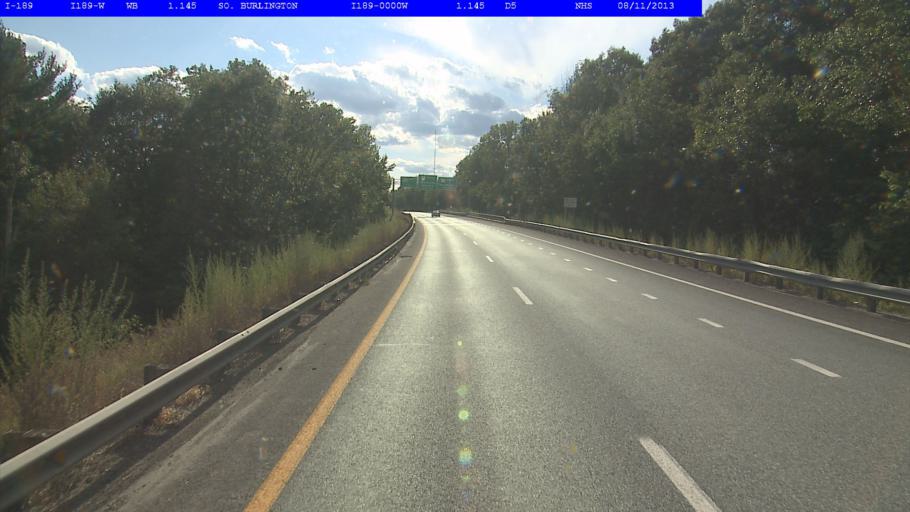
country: US
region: Vermont
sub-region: Chittenden County
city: South Burlington
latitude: 44.4519
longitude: -73.1875
